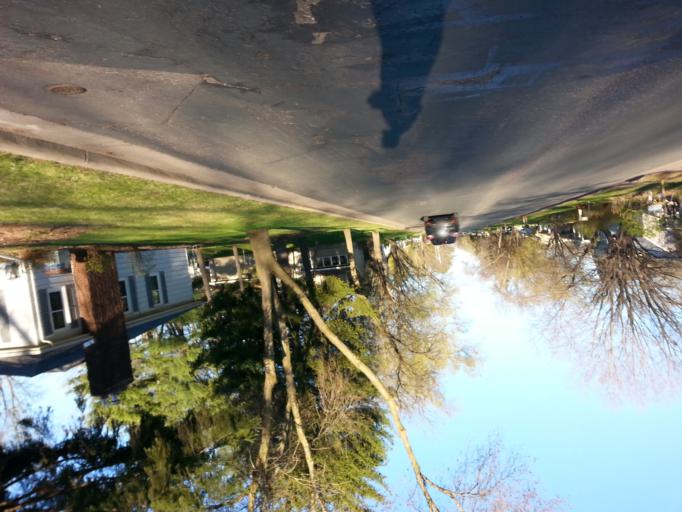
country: US
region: Wisconsin
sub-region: Saint Croix County
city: Hudson
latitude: 44.9704
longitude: -92.7491
